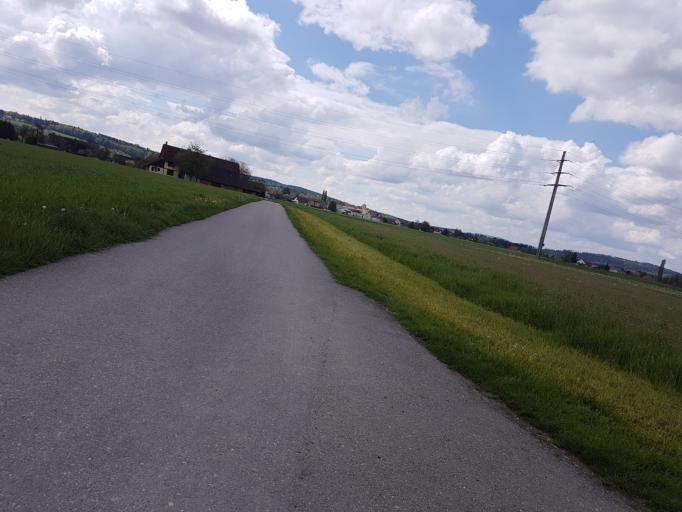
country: CH
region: Aargau
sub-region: Bezirk Zofingen
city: Fulenbach
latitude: 47.2845
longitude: 7.8367
